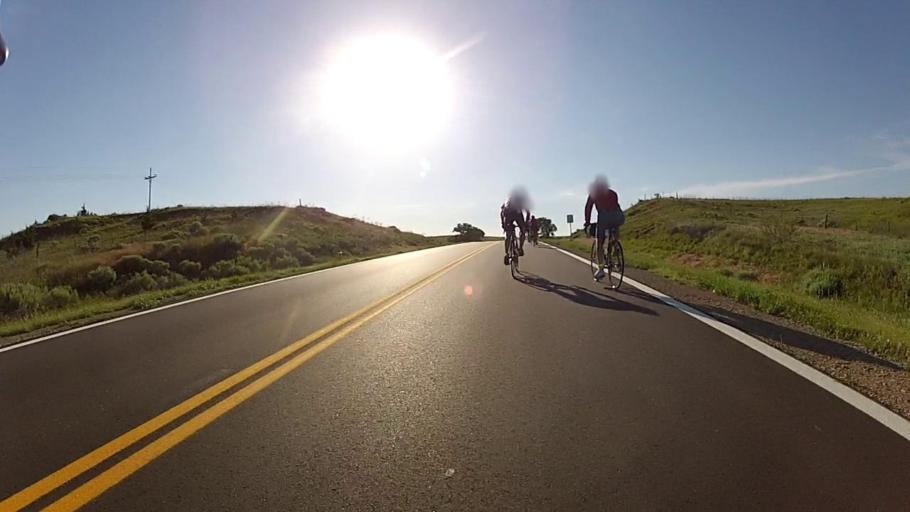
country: US
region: Kansas
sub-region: Comanche County
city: Coldwater
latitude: 37.2808
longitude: -99.0309
